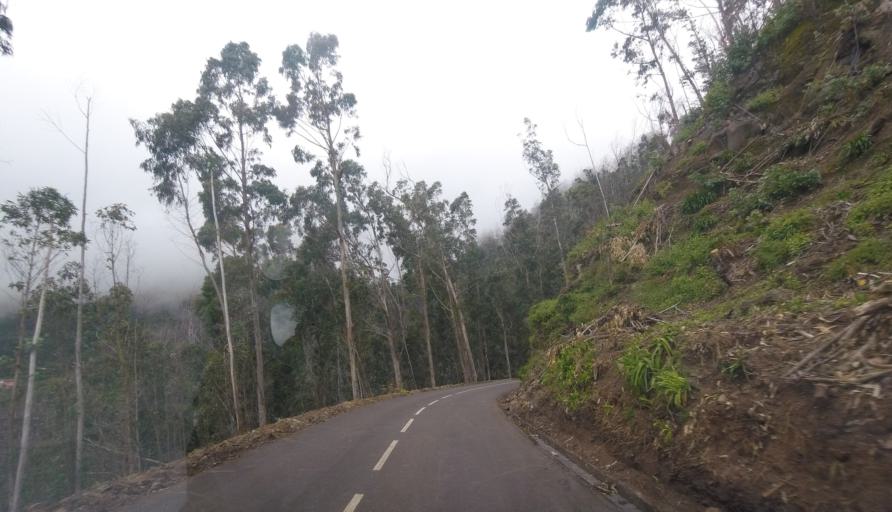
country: PT
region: Madeira
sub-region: Funchal
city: Nossa Senhora do Monte
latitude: 32.6867
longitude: -16.8903
